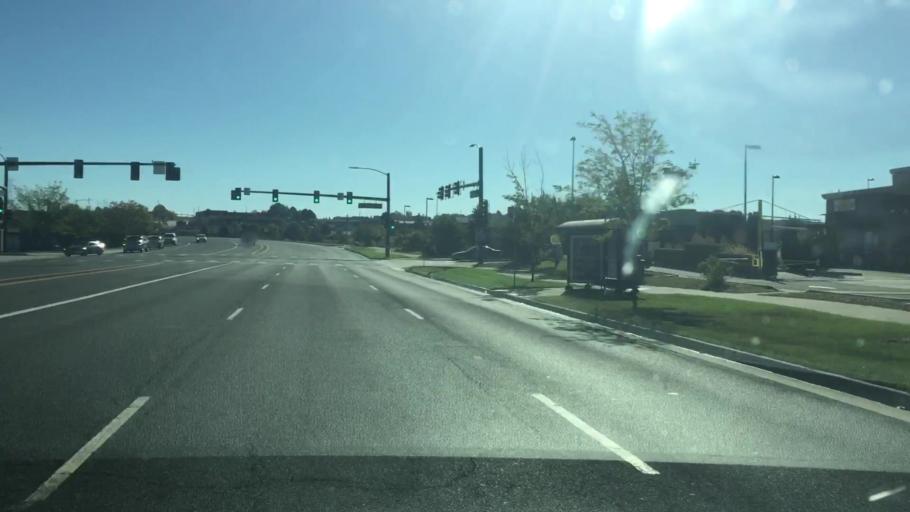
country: US
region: Colorado
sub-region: Douglas County
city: Parker
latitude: 39.5103
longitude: -104.7680
